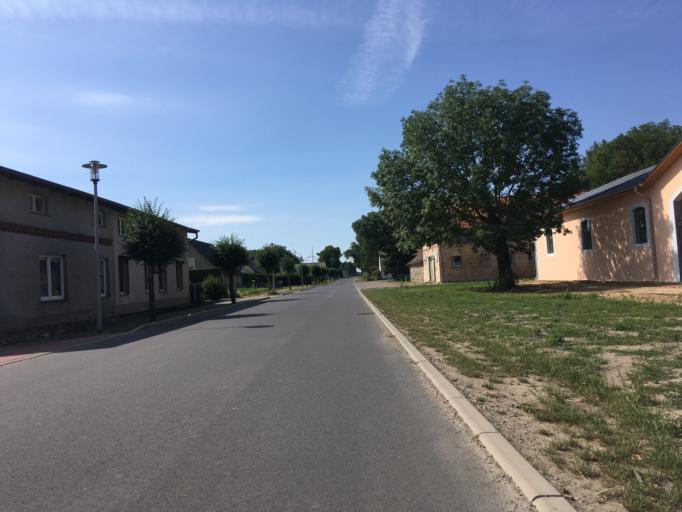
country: DE
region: Brandenburg
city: Grunow
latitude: 53.3005
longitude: 14.0409
